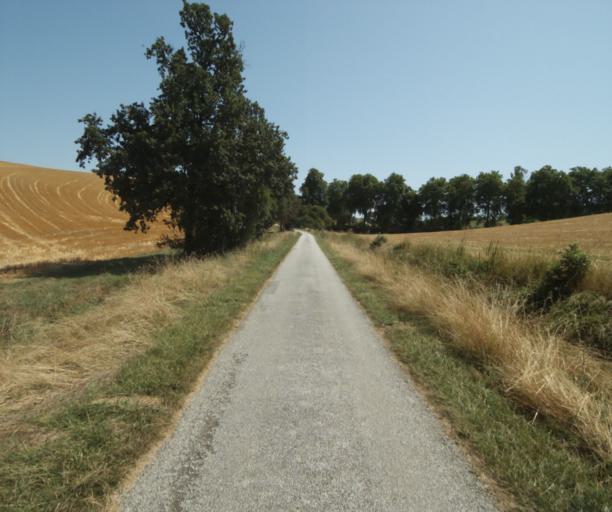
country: FR
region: Midi-Pyrenees
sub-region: Departement de la Haute-Garonne
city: Saint-Felix-Lauragais
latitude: 43.4629
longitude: 1.8568
